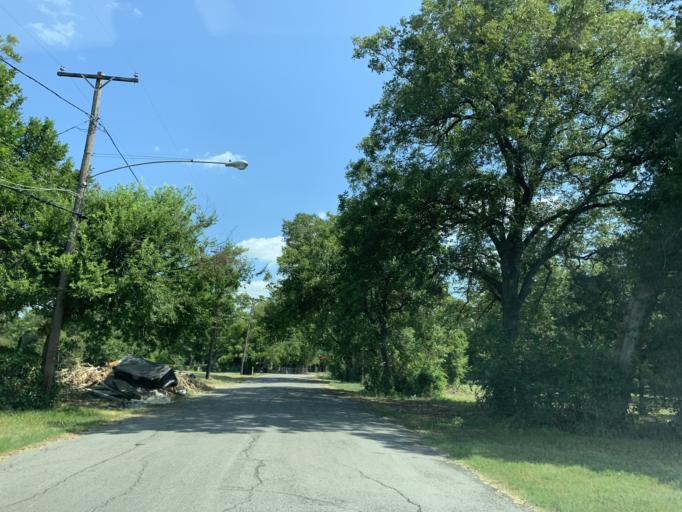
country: US
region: Texas
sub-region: Dallas County
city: Hutchins
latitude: 32.7071
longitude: -96.7658
